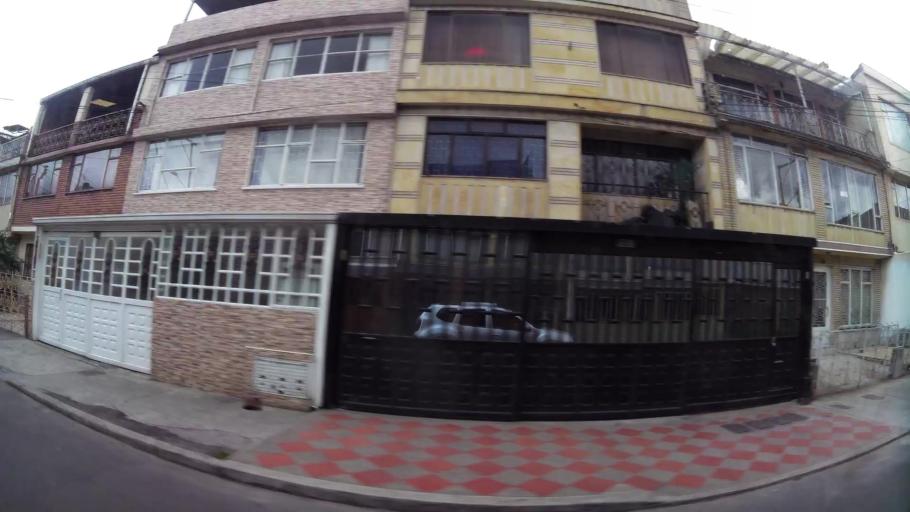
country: CO
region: Bogota D.C.
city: Bogota
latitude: 4.6242
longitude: -74.1148
